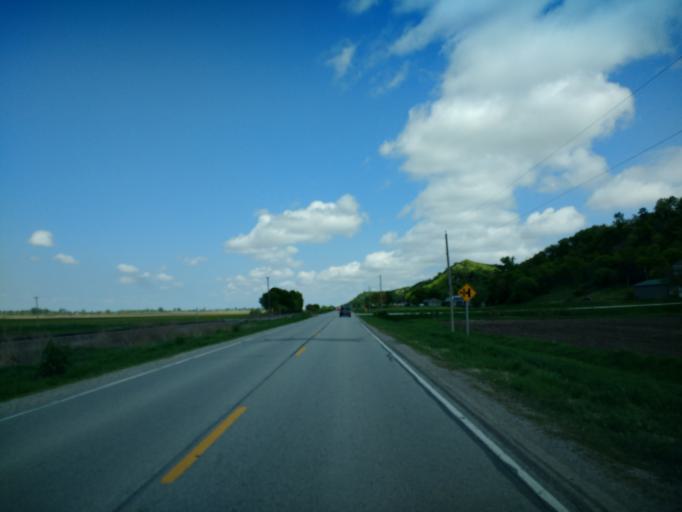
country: US
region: Iowa
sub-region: Harrison County
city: Missouri Valley
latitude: 41.4674
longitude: -95.8790
